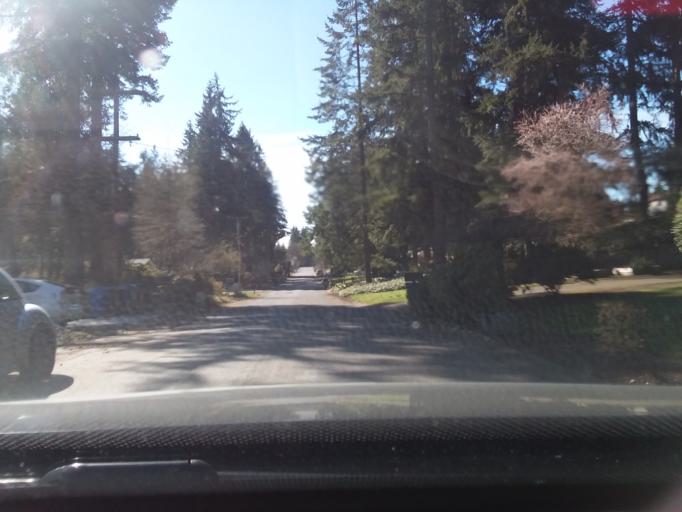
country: US
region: Washington
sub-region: Pierce County
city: Summit
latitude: 47.1655
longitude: -122.3436
